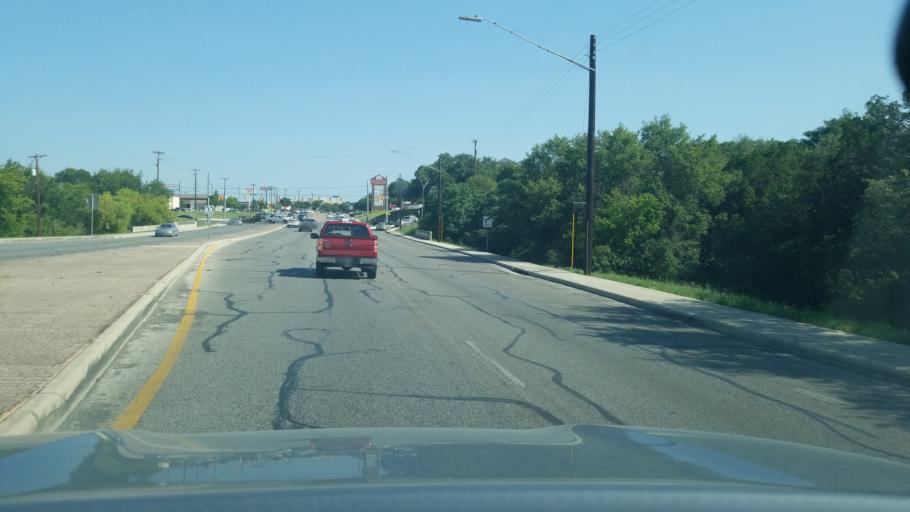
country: US
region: Texas
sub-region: Bexar County
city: Hollywood Park
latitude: 29.5805
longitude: -98.5151
